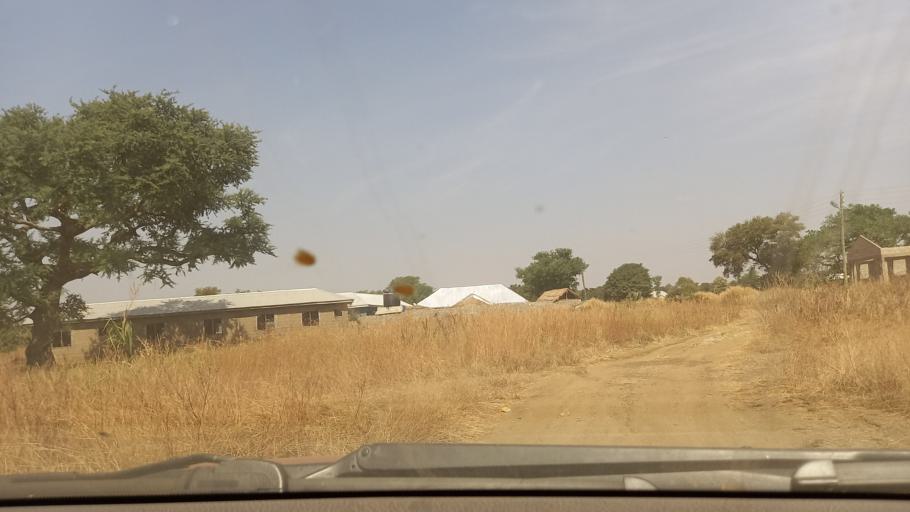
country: GH
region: Upper East
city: Navrongo
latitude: 10.8602
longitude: -1.0866
